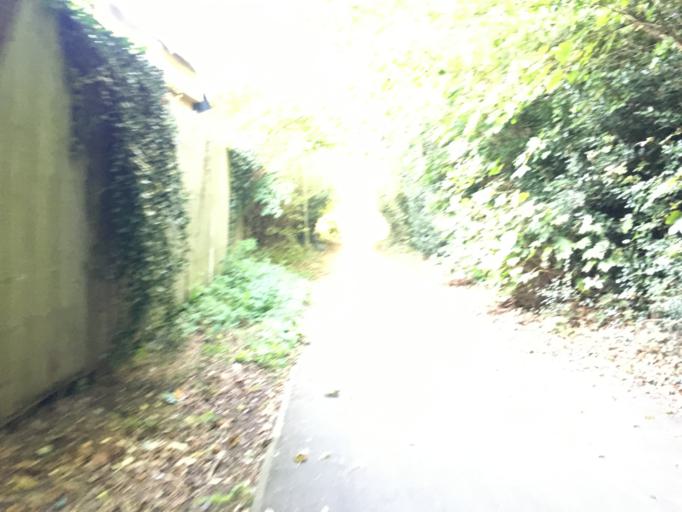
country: GB
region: England
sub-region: Warwickshire
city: Bedworth
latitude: 52.4781
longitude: -1.4246
